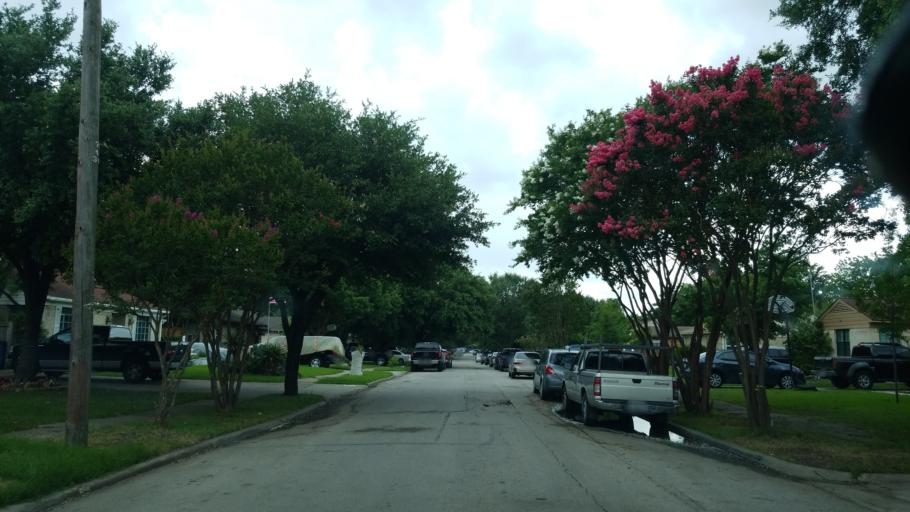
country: US
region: Texas
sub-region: Dallas County
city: Farmers Branch
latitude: 32.8787
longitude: -96.8595
